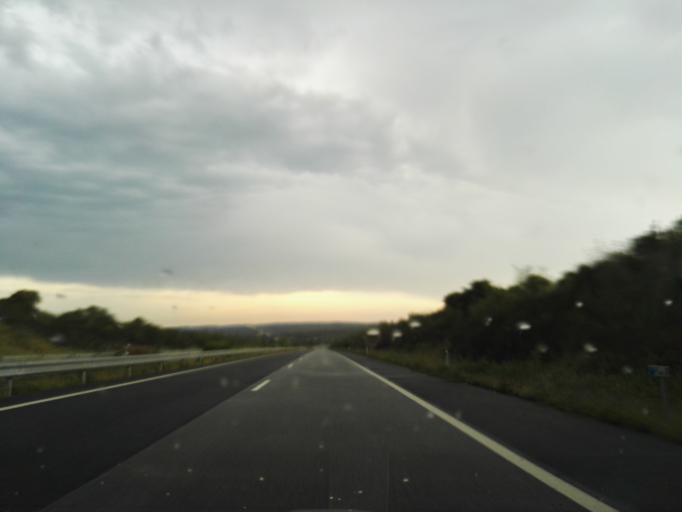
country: PT
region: Evora
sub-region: Evora
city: Evora
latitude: 38.6181
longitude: -7.9903
